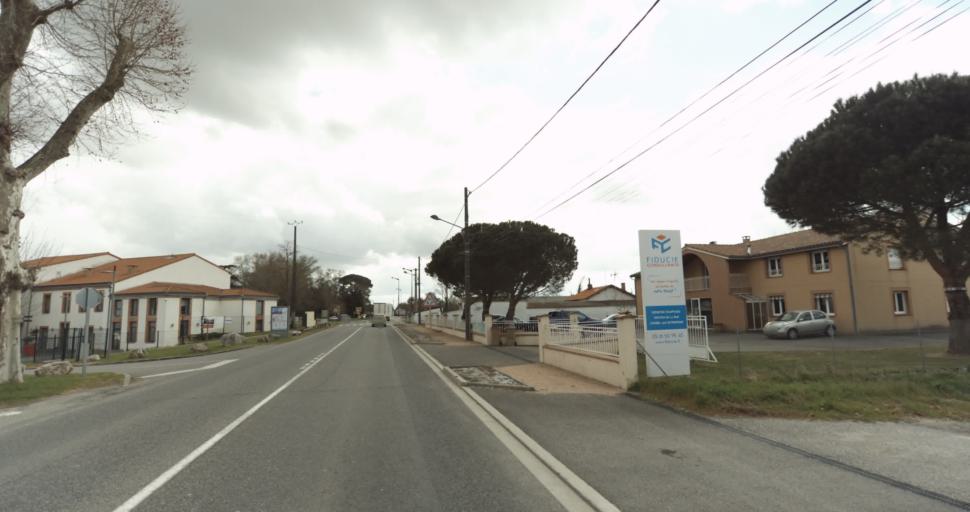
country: FR
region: Midi-Pyrenees
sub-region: Departement de la Haute-Garonne
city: Auterive
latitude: 43.3445
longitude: 1.4750
